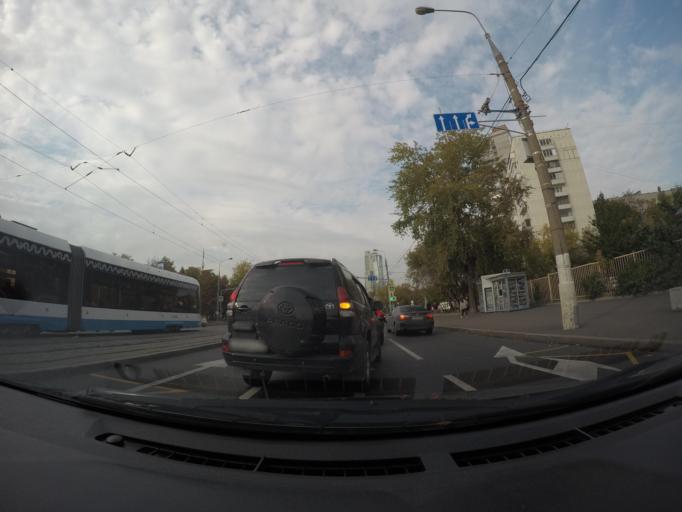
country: RU
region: Moscow
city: Lefortovo
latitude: 55.7775
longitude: 37.7218
